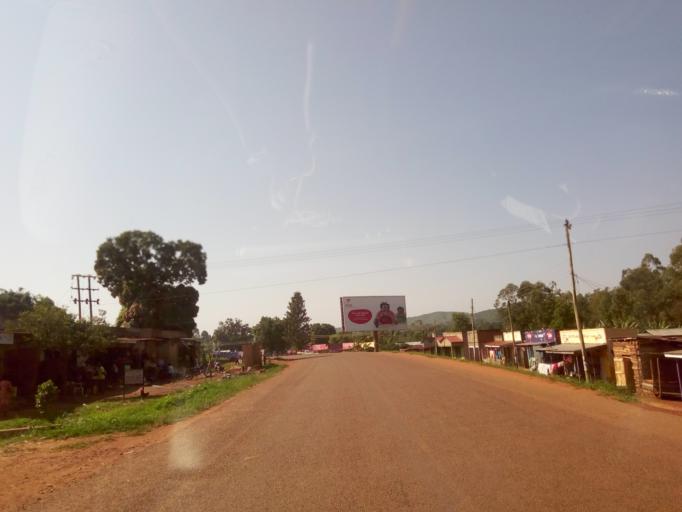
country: UG
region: Western Region
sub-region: Masindi District
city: Masindi
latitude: 1.6776
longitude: 31.7291
